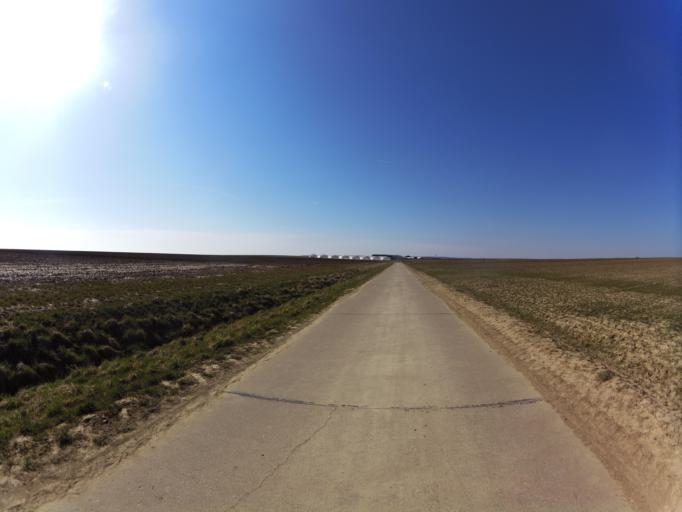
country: DE
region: Bavaria
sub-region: Regierungsbezirk Unterfranken
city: Oberpleichfeld
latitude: 49.8851
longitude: 10.0738
